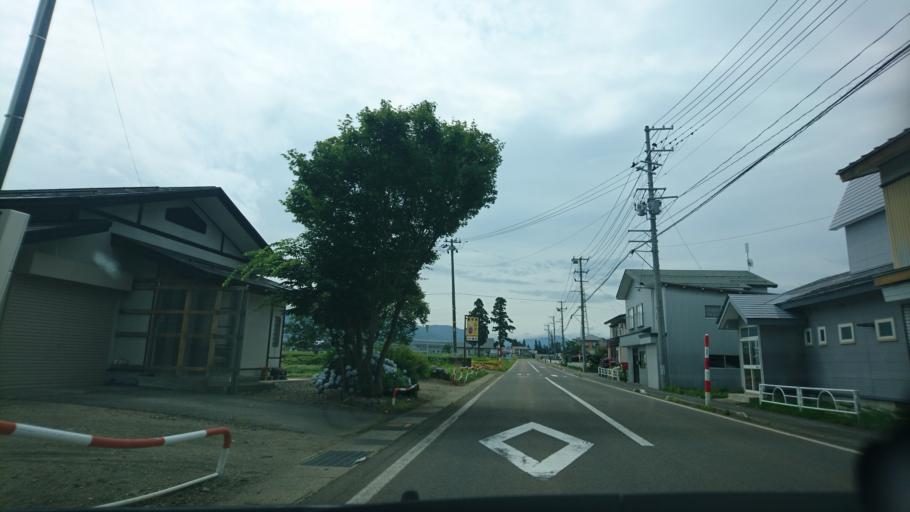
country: JP
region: Akita
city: Yuzawa
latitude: 39.1838
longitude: 140.5536
